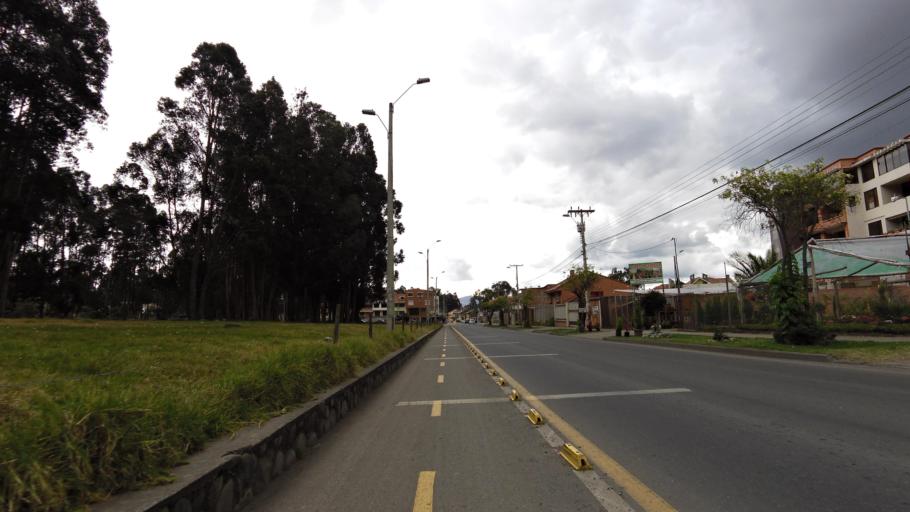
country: EC
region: Azuay
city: Cuenca
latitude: -2.9081
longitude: -79.0303
